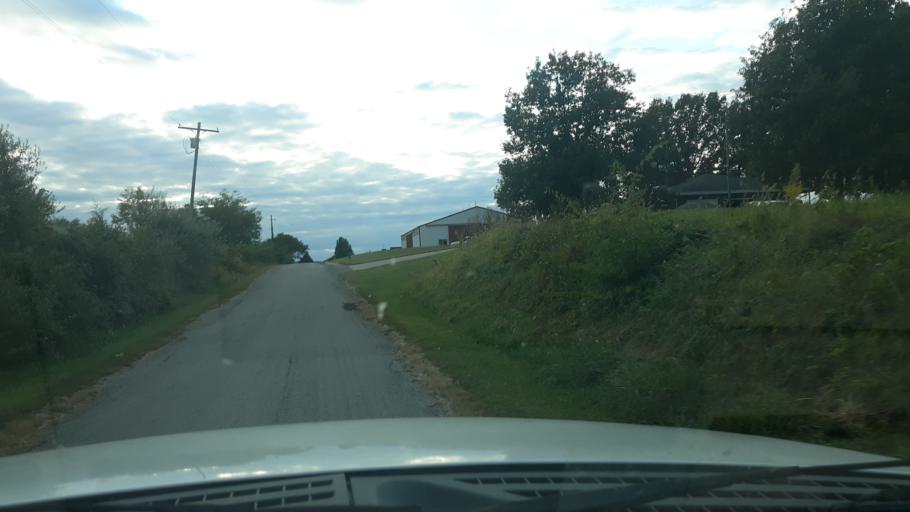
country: US
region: Illinois
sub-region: Saline County
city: Eldorado
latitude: 37.8378
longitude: -88.4638
